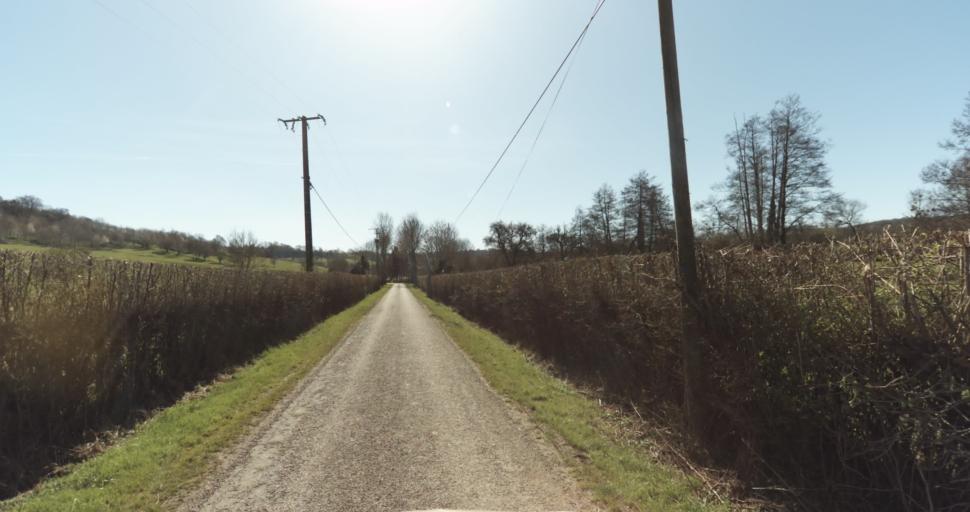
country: FR
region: Lower Normandy
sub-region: Departement du Calvados
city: Livarot
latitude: 48.9593
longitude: 0.0696
